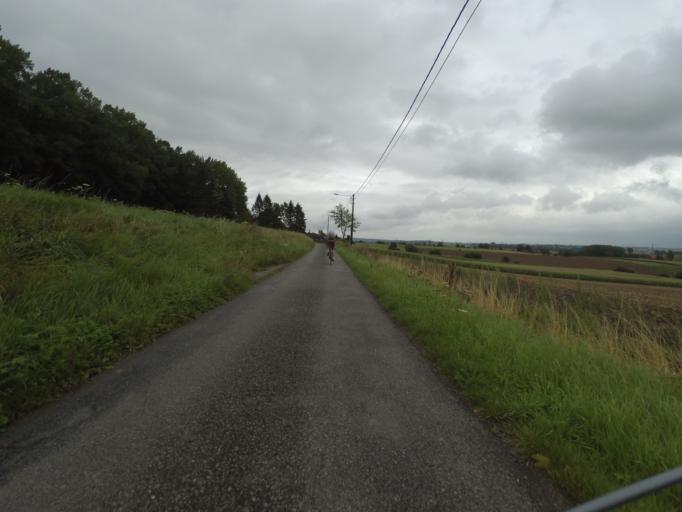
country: BE
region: Wallonia
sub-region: Province du Hainaut
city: Frasnes-lez-Buissenal
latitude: 50.6343
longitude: 3.5635
